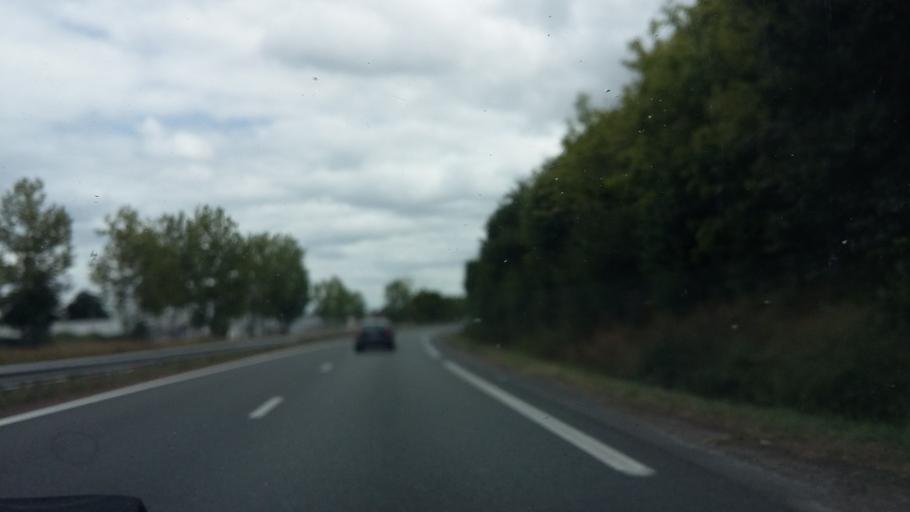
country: FR
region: Pays de la Loire
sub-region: Departement de la Vendee
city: La Genetouze
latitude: 46.7238
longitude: -1.5574
